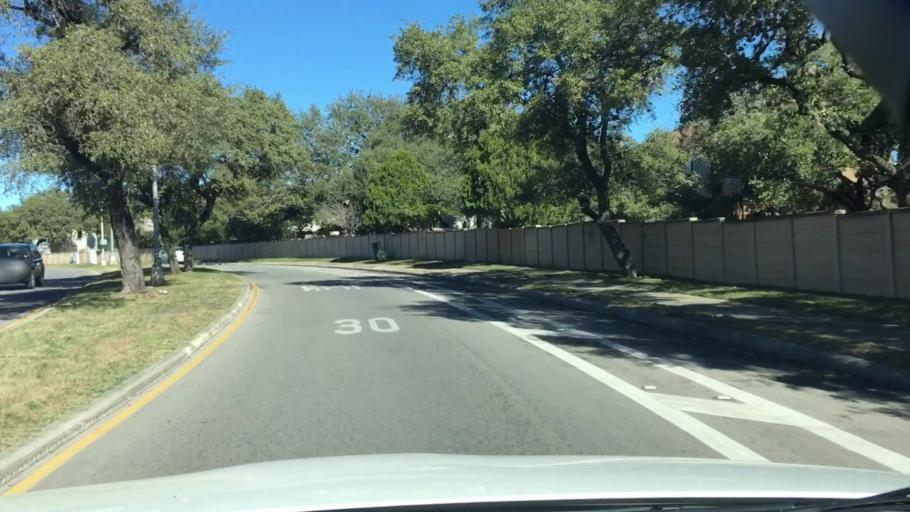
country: US
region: Texas
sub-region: Bexar County
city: Hollywood Park
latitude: 29.6002
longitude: -98.4569
